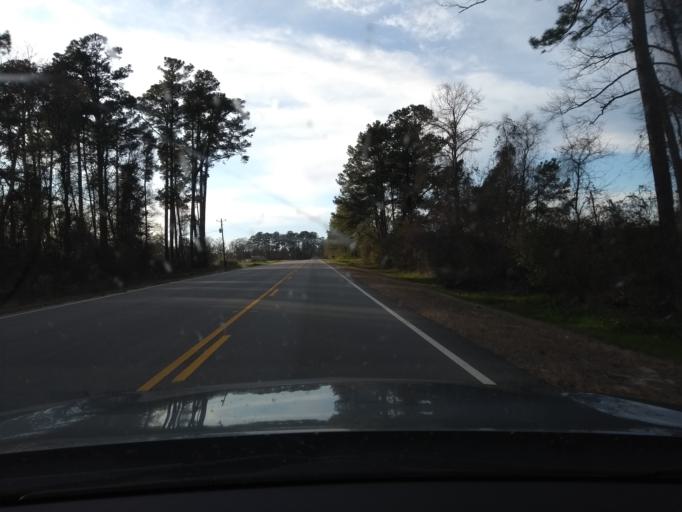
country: US
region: Georgia
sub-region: Bulloch County
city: Brooklet
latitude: 32.2927
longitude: -81.7660
